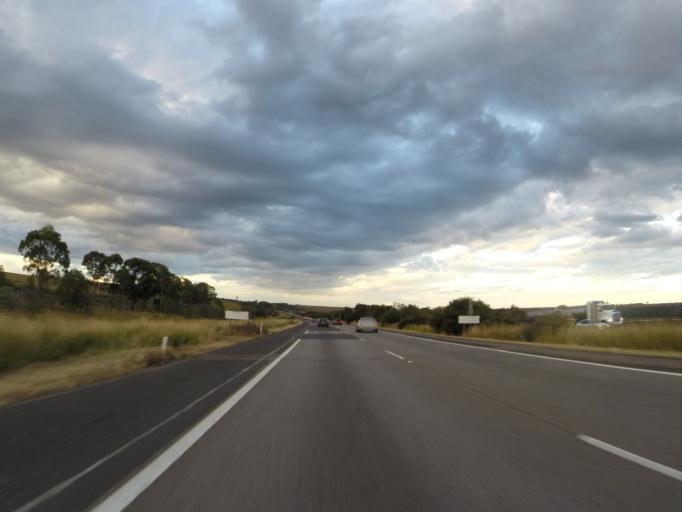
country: AU
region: New South Wales
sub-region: Wollondilly
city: Douglas Park
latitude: -34.1707
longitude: 150.7337
